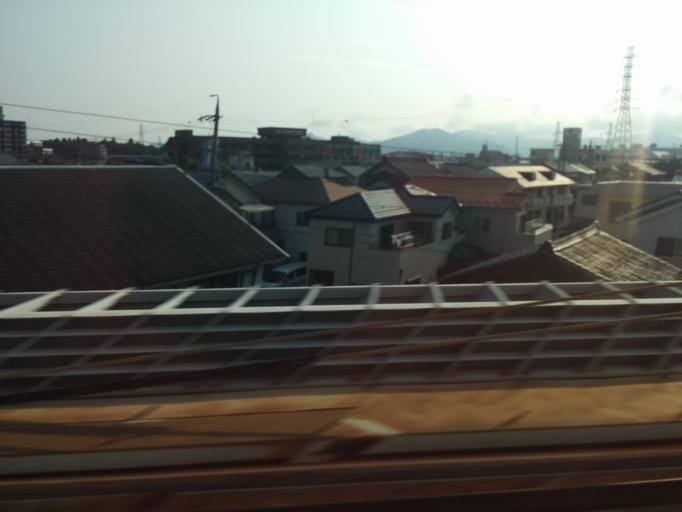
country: JP
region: Aichi
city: Toyohashi
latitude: 34.7480
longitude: 137.3911
